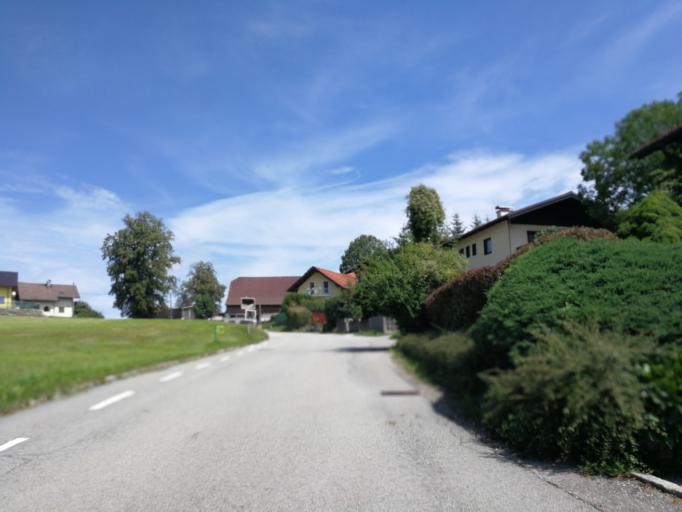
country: AT
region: Salzburg
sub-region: Politischer Bezirk Salzburg-Umgebung
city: Hallwang
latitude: 47.8437
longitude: 13.0681
